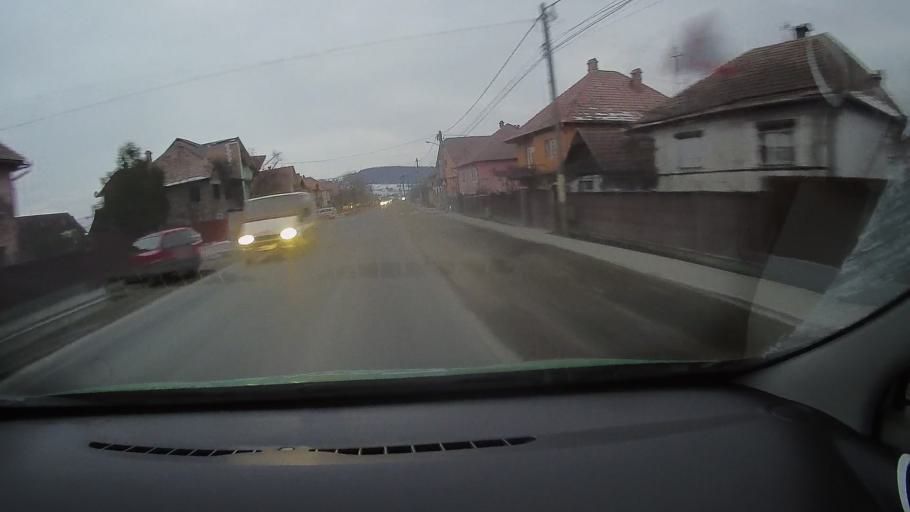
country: RO
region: Harghita
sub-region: Comuna Feliceni
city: Feliceni
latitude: 46.2702
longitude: 25.2751
